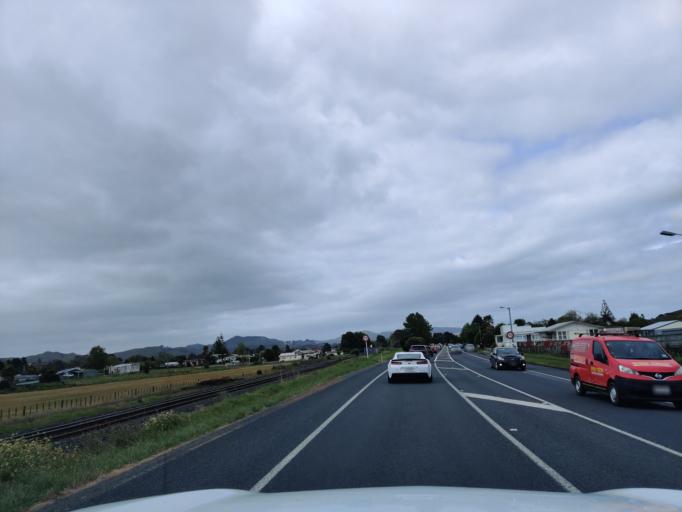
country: NZ
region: Waikato
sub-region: Waikato District
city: Ngaruawahia
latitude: -37.5341
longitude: 175.1592
